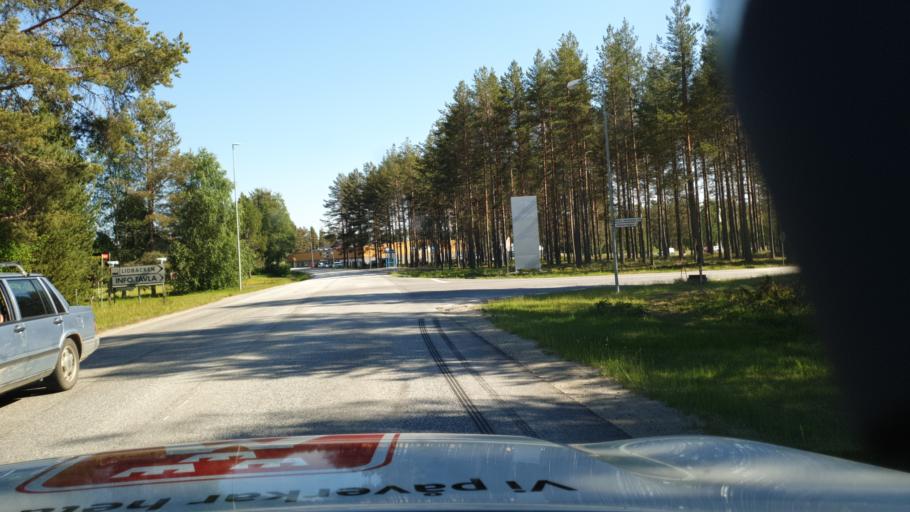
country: SE
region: Vaesterbotten
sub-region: Vindelns Kommun
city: Vindeln
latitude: 64.1831
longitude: 19.7084
